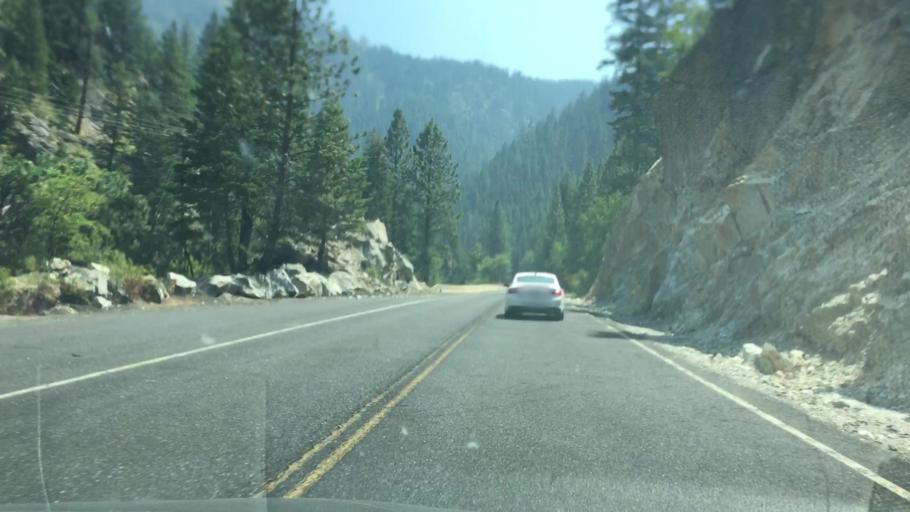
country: US
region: Idaho
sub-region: Valley County
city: McCall
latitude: 45.1423
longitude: -116.2883
